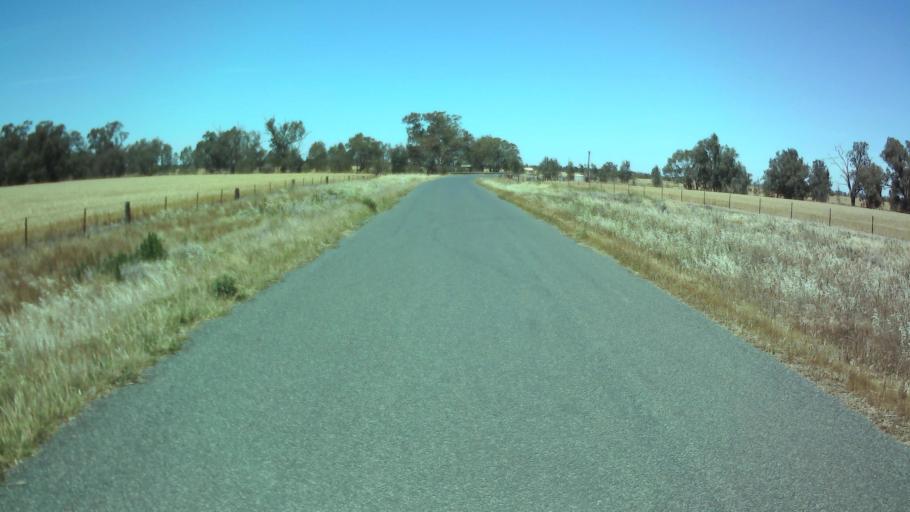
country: AU
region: New South Wales
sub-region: Weddin
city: Grenfell
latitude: -34.0372
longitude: 147.7898
